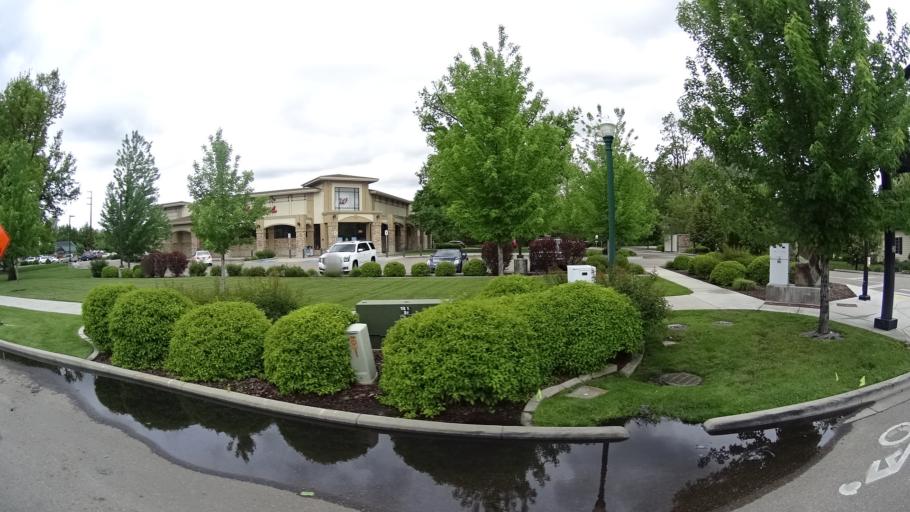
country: US
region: Idaho
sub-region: Ada County
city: Eagle
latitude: 43.6927
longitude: -116.3541
